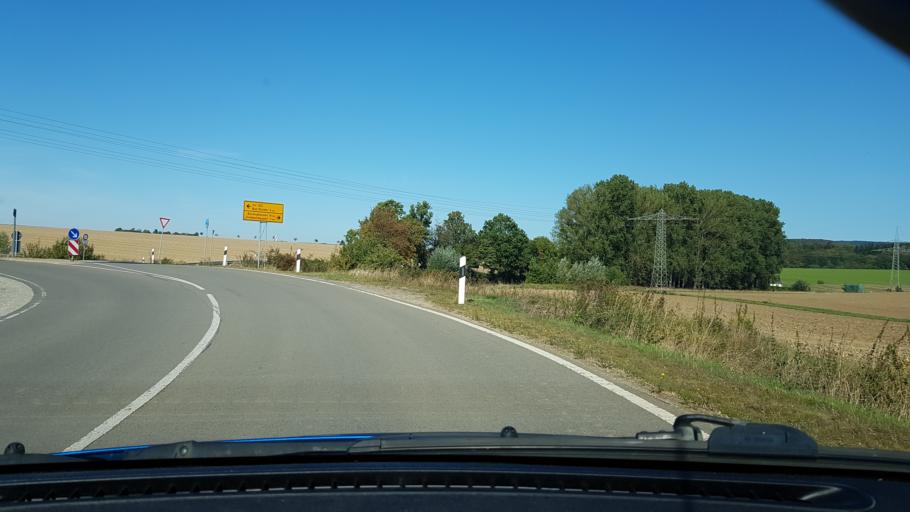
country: DE
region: Lower Saxony
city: Bad Munder am Deister
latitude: 52.2226
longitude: 9.4367
